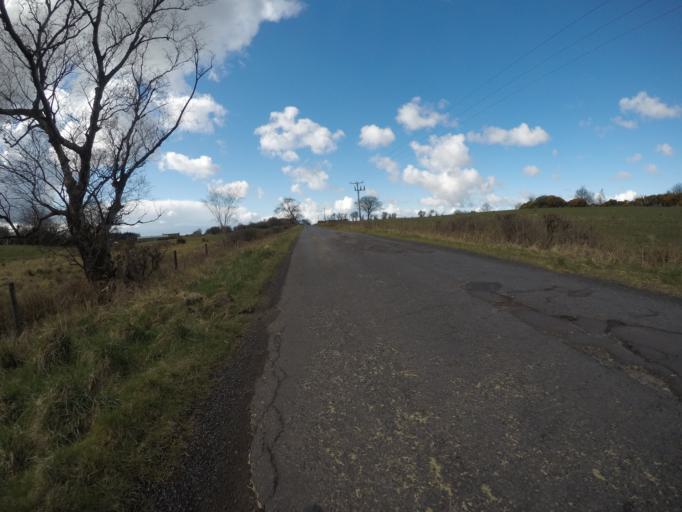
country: GB
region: Scotland
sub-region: North Ayrshire
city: Kilbirnie
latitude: 55.7161
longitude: -4.6827
